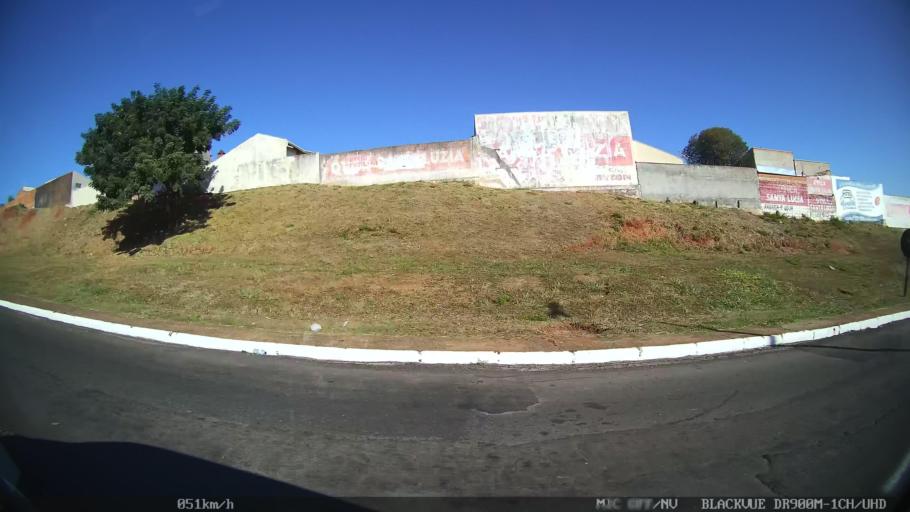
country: BR
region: Sao Paulo
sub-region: Olimpia
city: Olimpia
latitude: -20.7390
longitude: -48.9018
